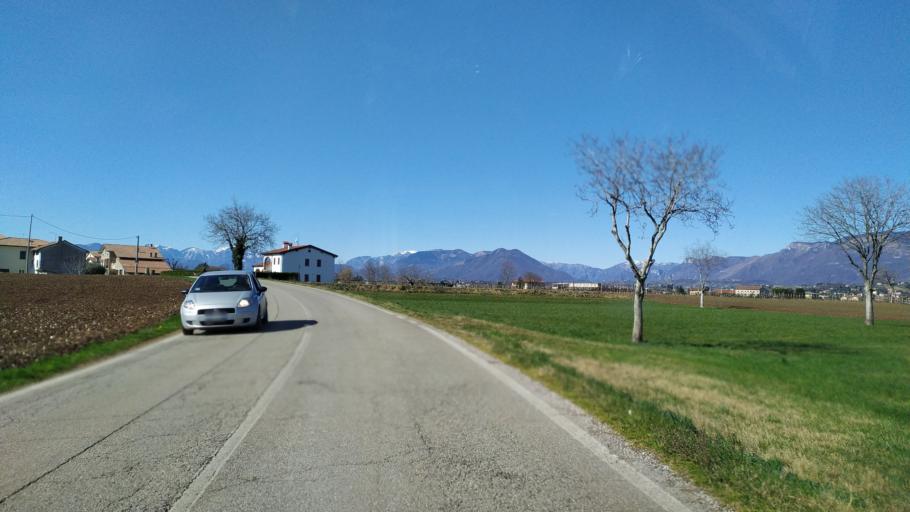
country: IT
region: Veneto
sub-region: Provincia di Vicenza
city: Breganze
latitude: 45.6894
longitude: 11.5848
